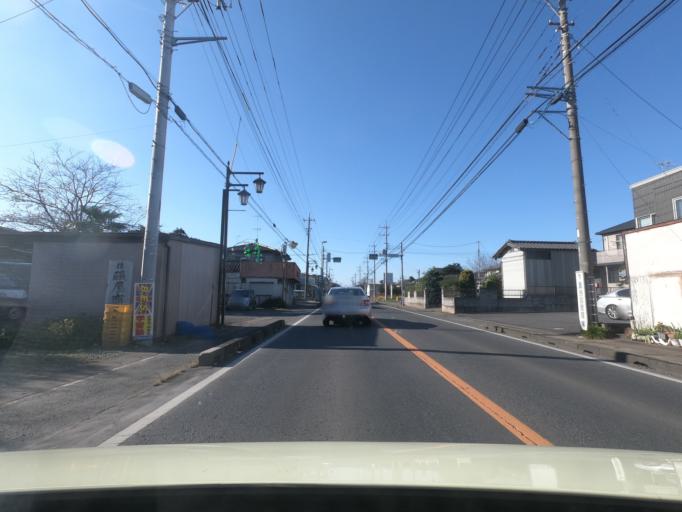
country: JP
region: Ibaraki
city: Ishige
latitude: 36.1851
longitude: 139.9458
